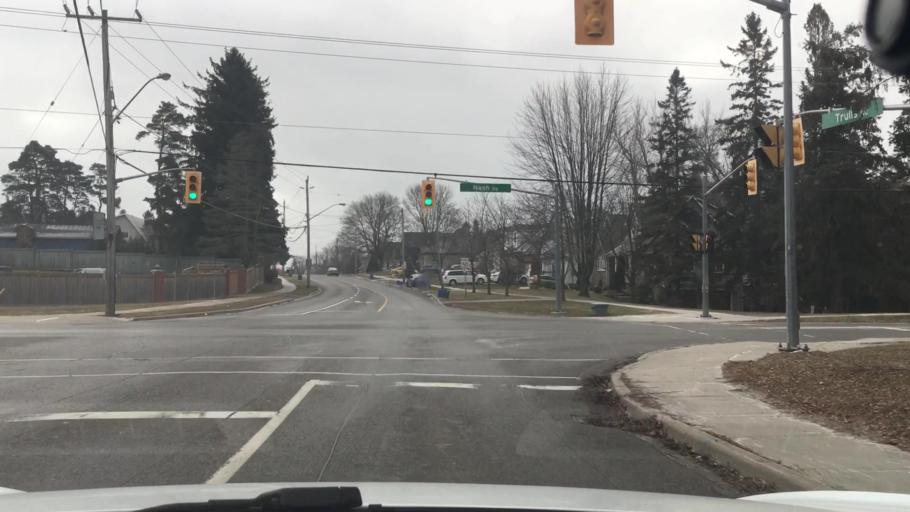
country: CA
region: Ontario
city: Oshawa
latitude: 43.9141
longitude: -78.7897
